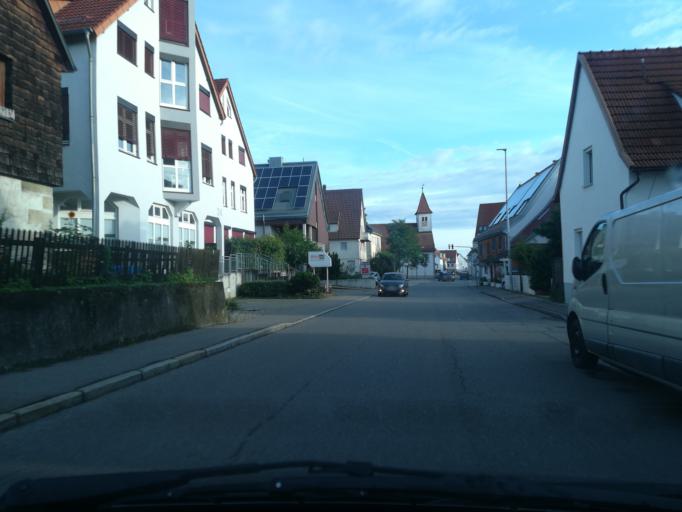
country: DE
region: Baden-Wuerttemberg
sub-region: Tuebingen Region
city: Sickenhausen
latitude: 48.5215
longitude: 9.1754
